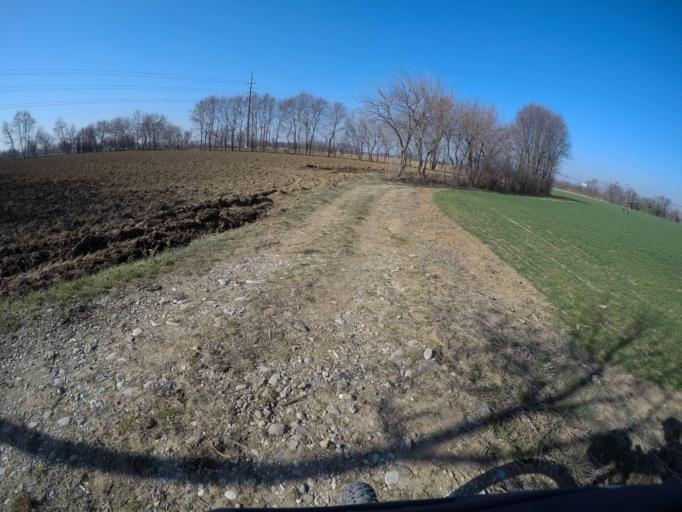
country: IT
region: Friuli Venezia Giulia
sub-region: Provincia di Udine
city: Pozzuolo del Friuli
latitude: 45.9841
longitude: 13.1646
